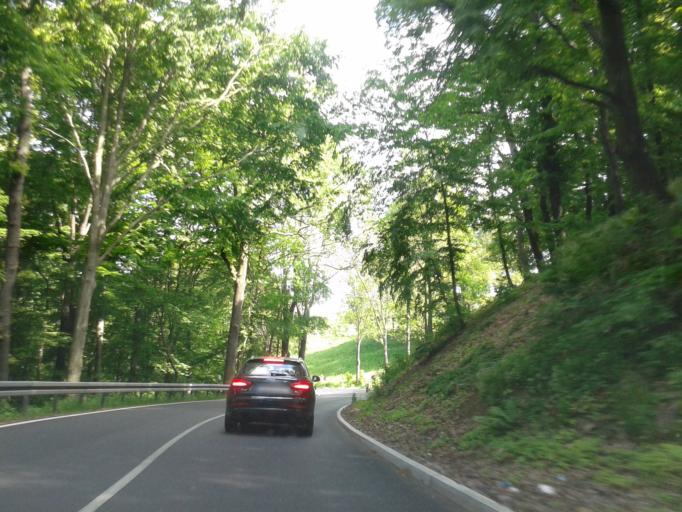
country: DE
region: Saxony
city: Nossen
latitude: 51.0225
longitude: 13.3261
